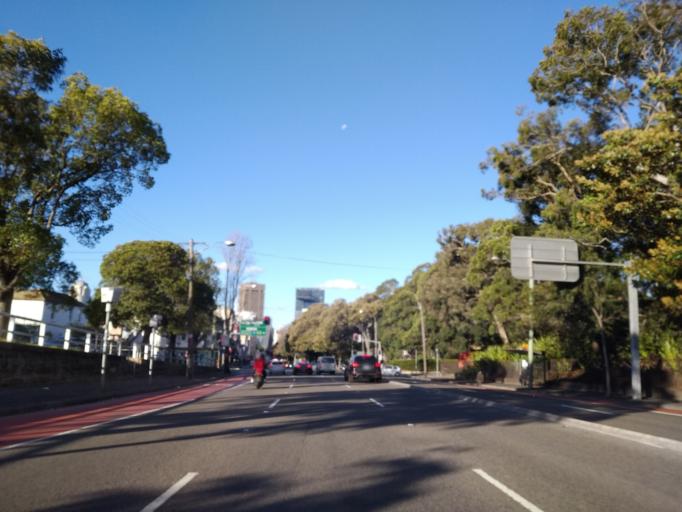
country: AU
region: New South Wales
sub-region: City of Sydney
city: Chippendale
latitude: -33.8848
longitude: 151.1906
